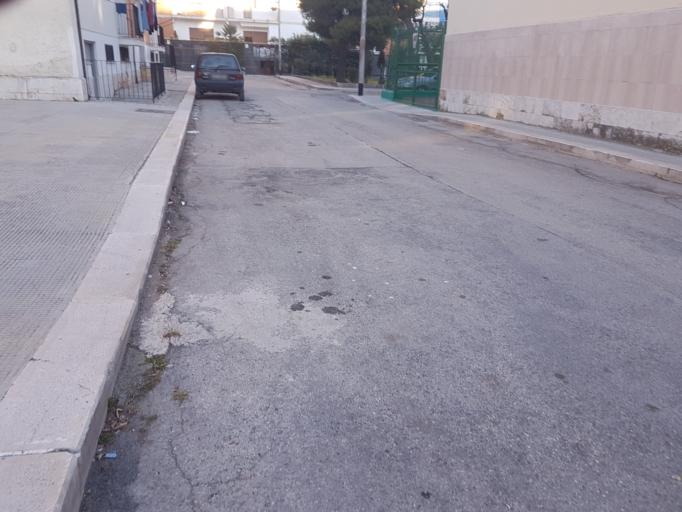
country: IT
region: Apulia
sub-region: Provincia di Bari
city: Corato
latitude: 41.1507
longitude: 16.4038
